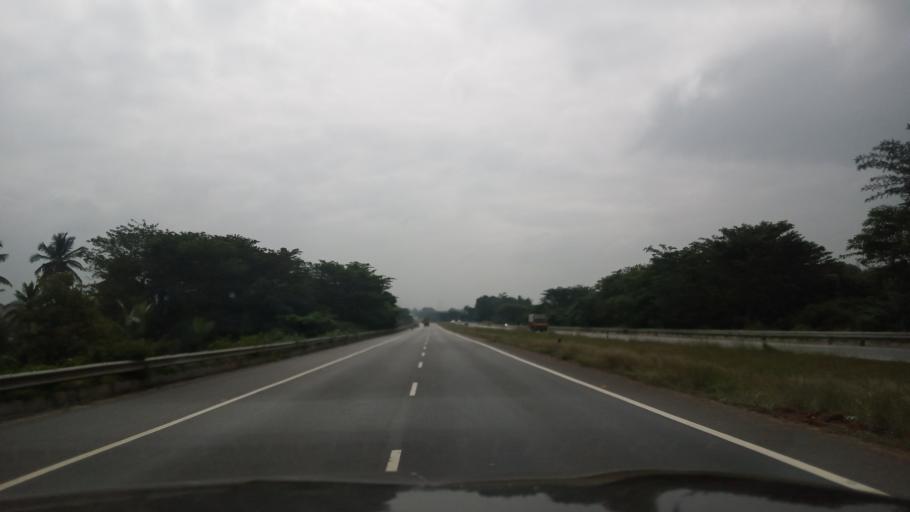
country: IN
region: Karnataka
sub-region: Bangalore Urban
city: Bangalore
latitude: 12.9431
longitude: 77.4698
